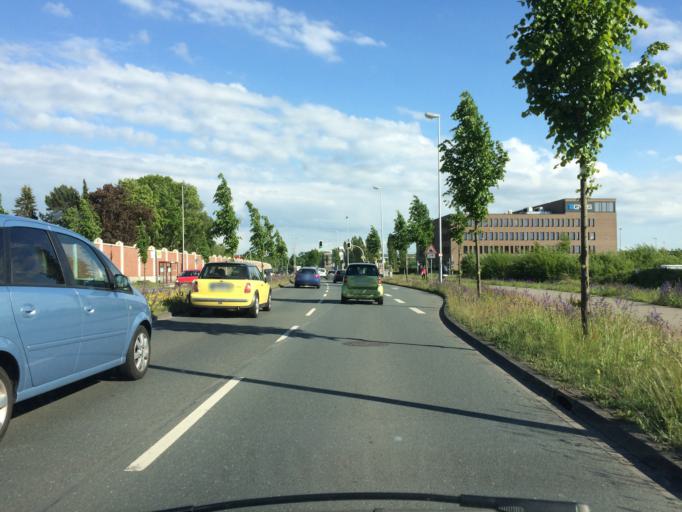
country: DE
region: North Rhine-Westphalia
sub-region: Regierungsbezirk Munster
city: Muenster
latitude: 51.9396
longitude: 7.6520
